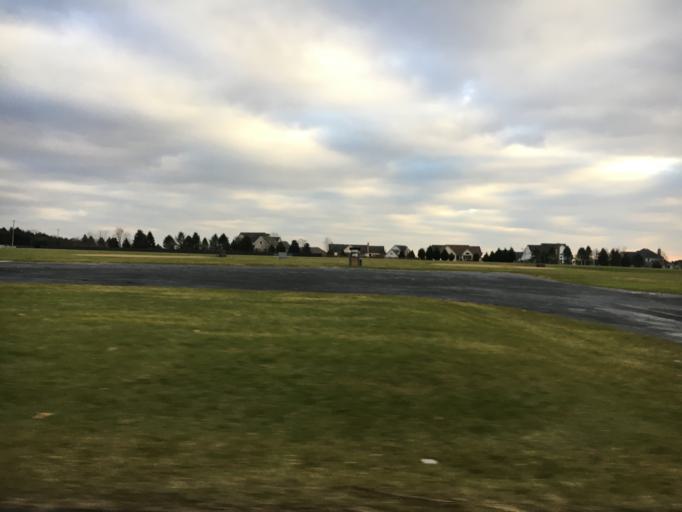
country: US
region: Pennsylvania
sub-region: Lehigh County
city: Schnecksville
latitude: 40.6951
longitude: -75.5938
